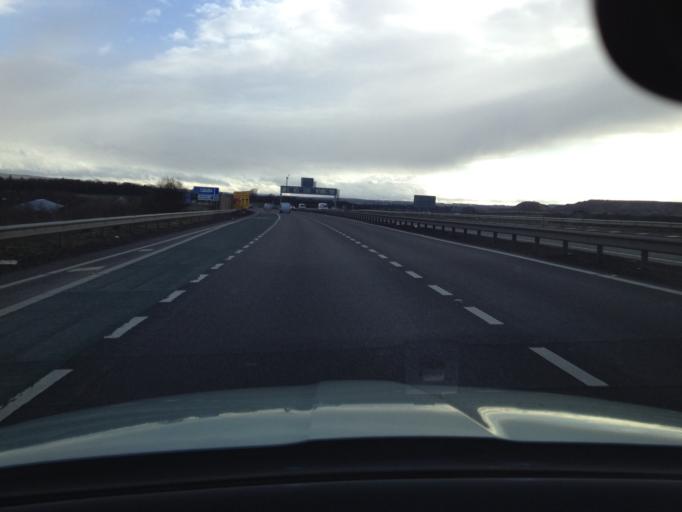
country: GB
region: Scotland
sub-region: Edinburgh
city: Kirkliston
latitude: 55.9615
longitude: -3.4132
